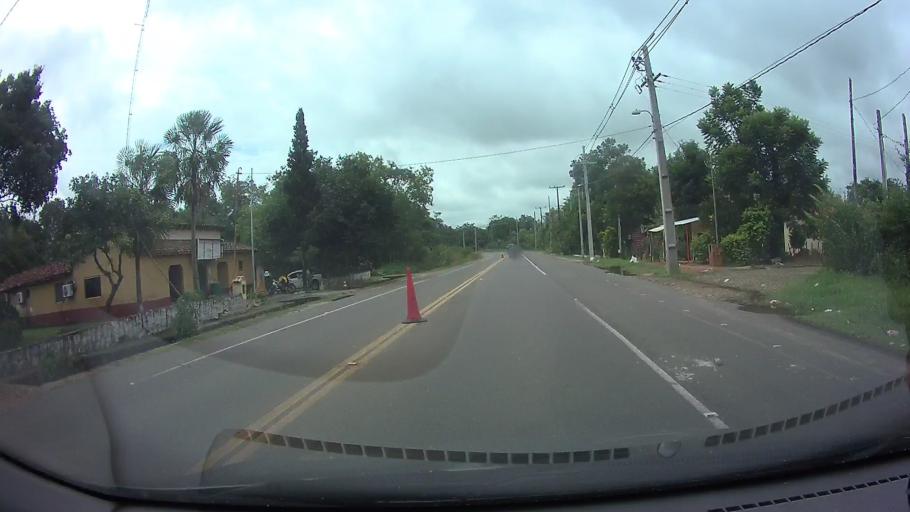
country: PY
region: Central
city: Limpio
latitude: -25.2180
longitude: -57.4173
